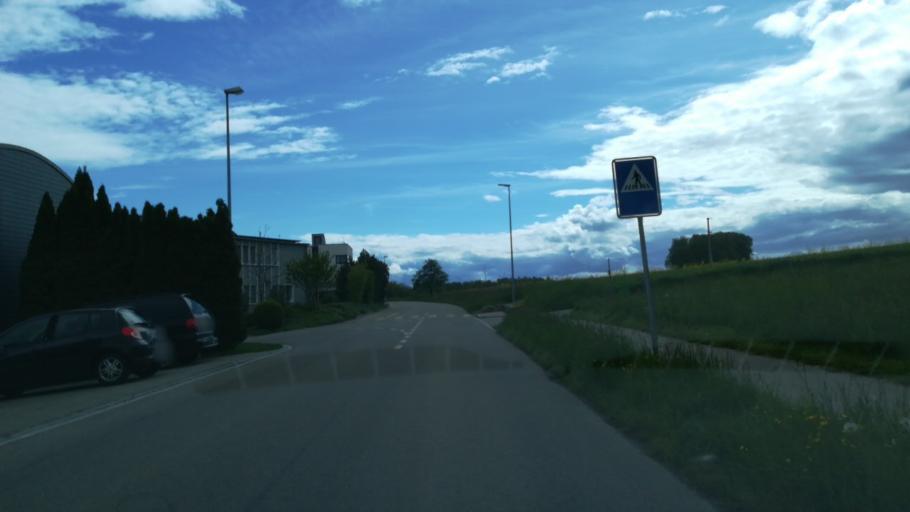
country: CH
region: Schaffhausen
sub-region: Bezirk Reiat
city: Stetten
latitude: 47.7367
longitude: 8.6569
